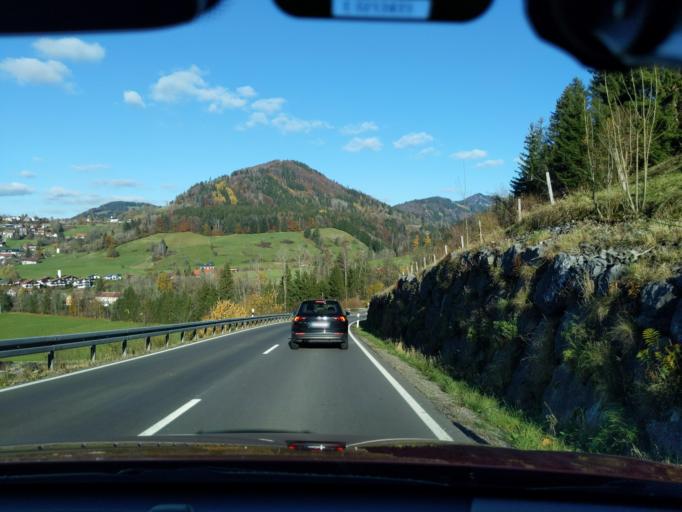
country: DE
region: Bavaria
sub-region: Swabia
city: Oberstaufen
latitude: 47.5382
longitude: 10.0198
